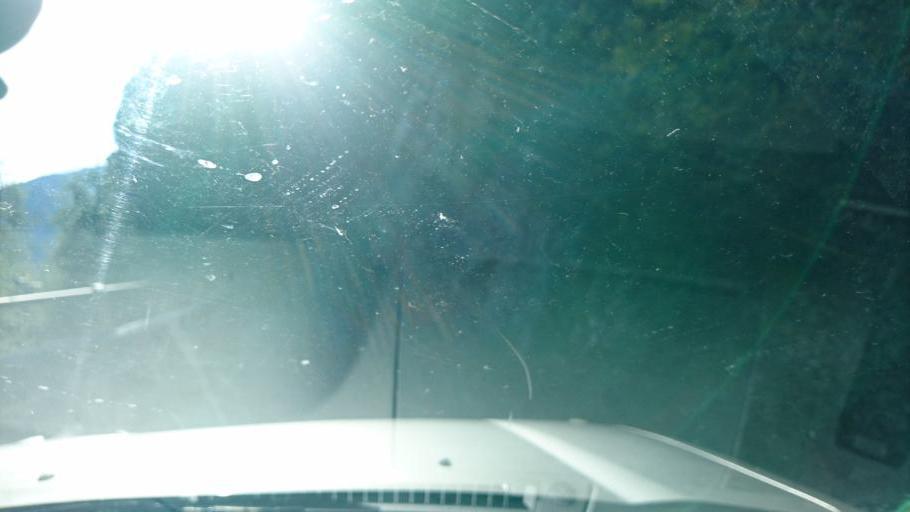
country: IT
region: Lombardy
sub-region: Provincia di Brescia
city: Lozio
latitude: 46.0464
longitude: 10.2202
